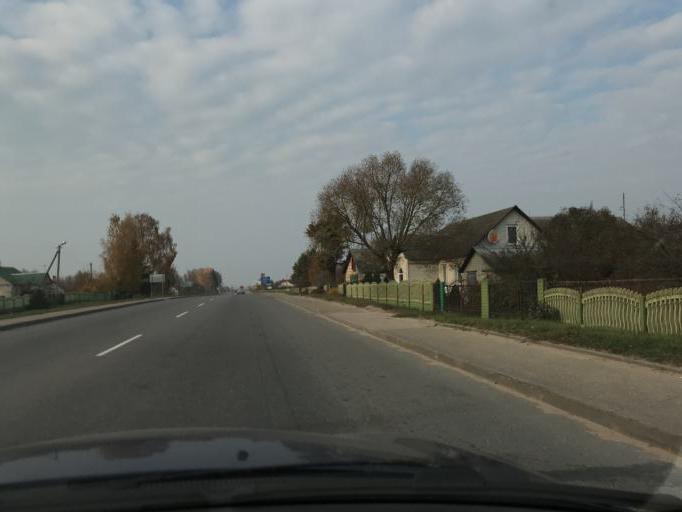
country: BY
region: Grodnenskaya
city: Lida
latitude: 53.8572
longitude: 25.3336
